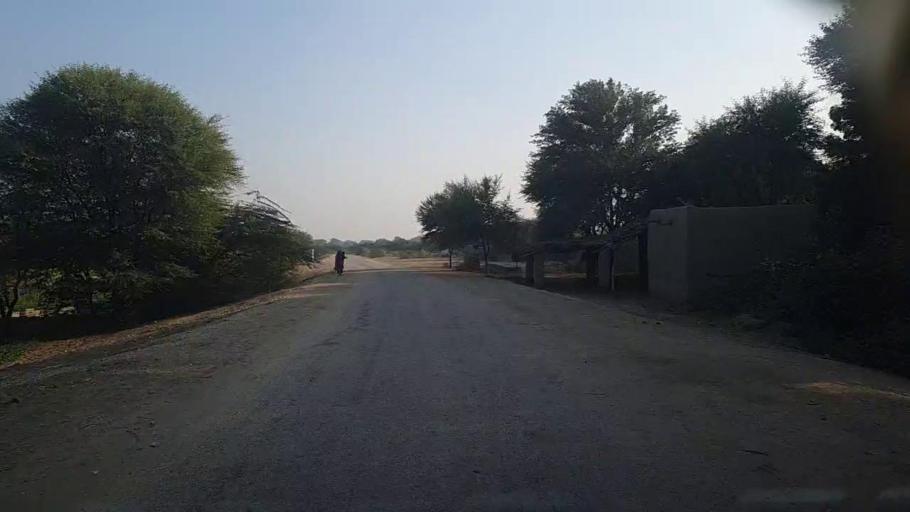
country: PK
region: Sindh
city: Karaundi
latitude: 26.7419
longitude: 68.4773
